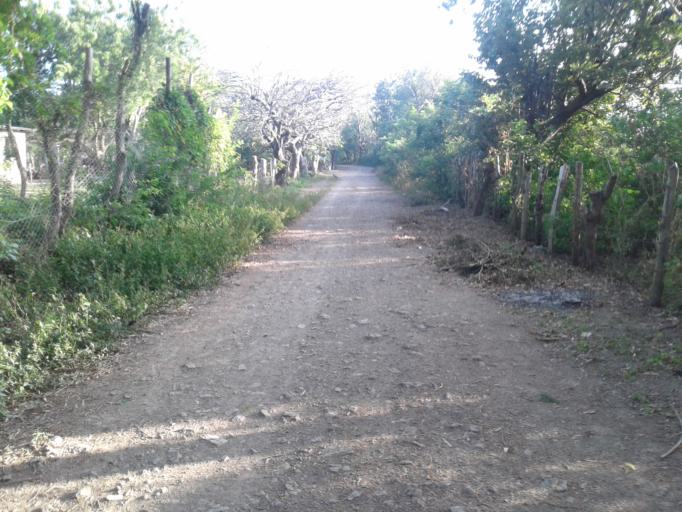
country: NI
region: Rivas
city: Tola
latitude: 11.4833
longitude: -86.1002
